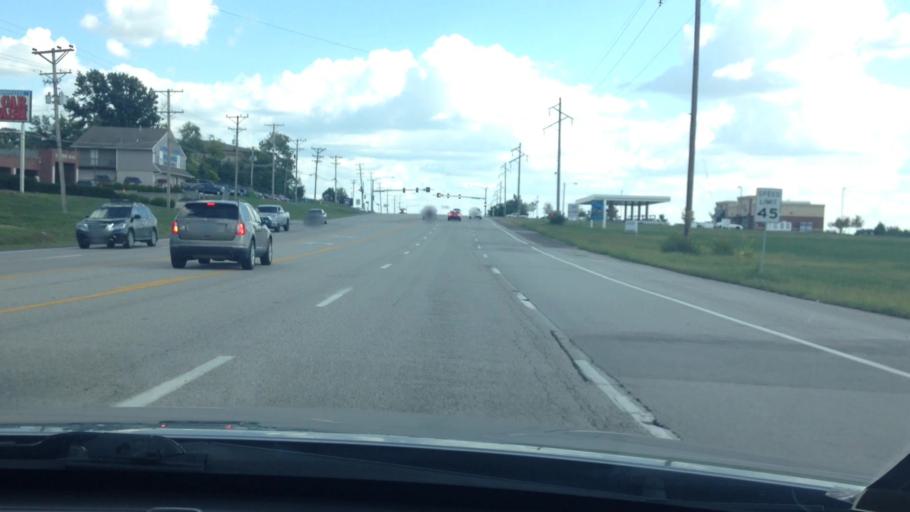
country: US
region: Missouri
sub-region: Clay County
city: Liberty
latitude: 39.2497
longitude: -94.4480
